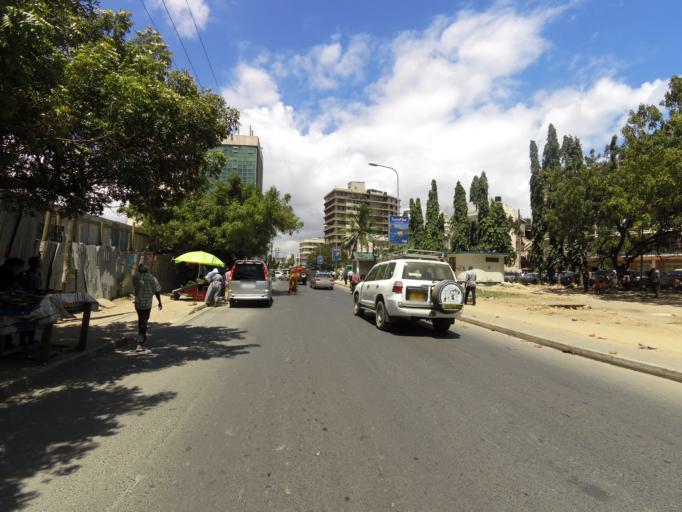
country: TZ
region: Dar es Salaam
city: Dar es Salaam
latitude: -6.8206
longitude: 39.2849
